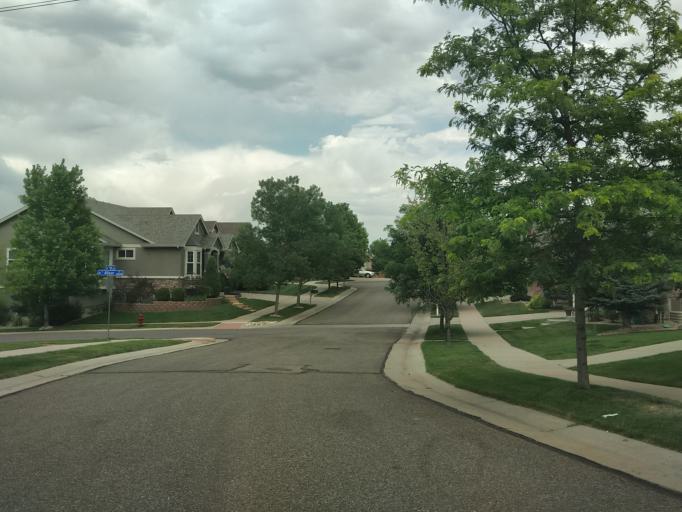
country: US
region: Colorado
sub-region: Jefferson County
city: Lakewood
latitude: 39.6987
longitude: -105.0866
